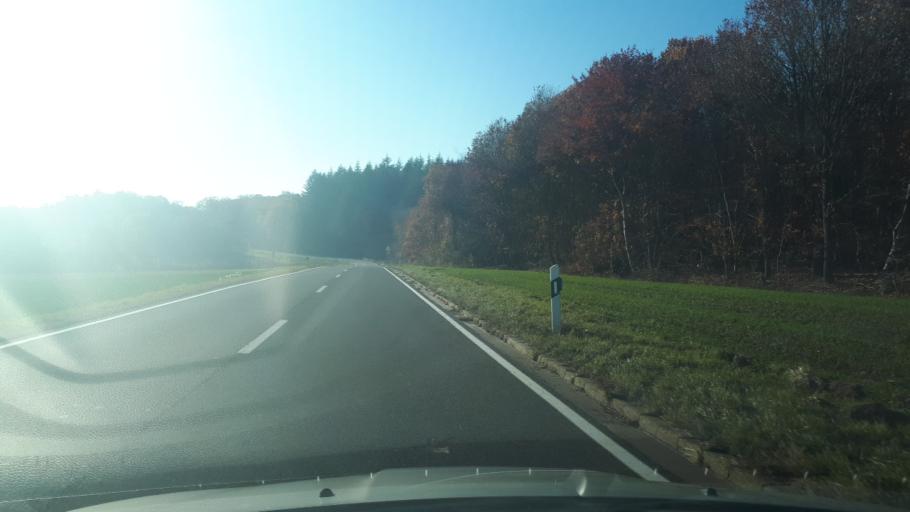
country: DE
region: Rheinland-Pfalz
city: Kliding
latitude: 50.1436
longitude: 7.0543
